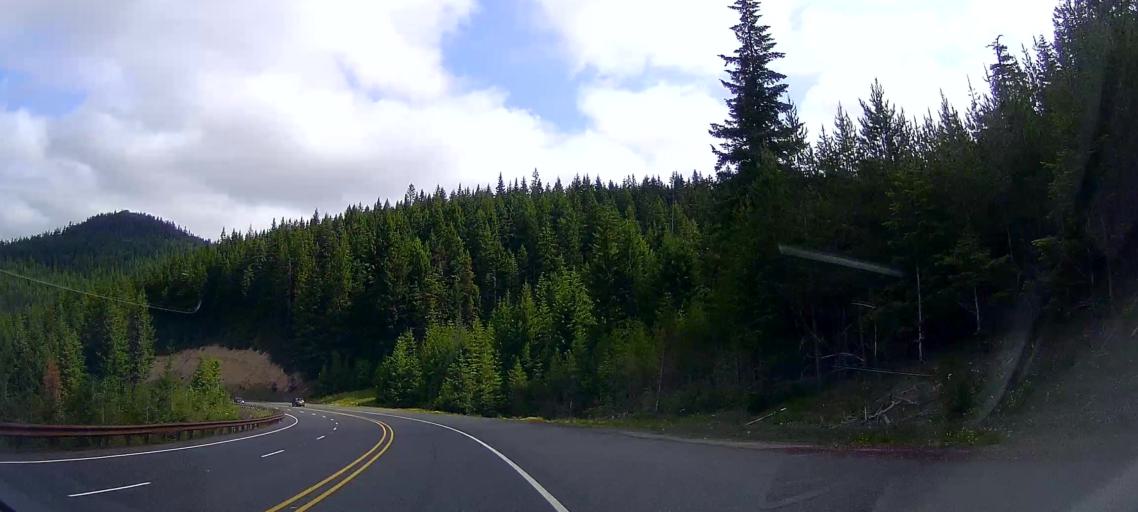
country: US
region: Oregon
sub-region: Clackamas County
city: Mount Hood Village
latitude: 45.2361
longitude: -121.6982
